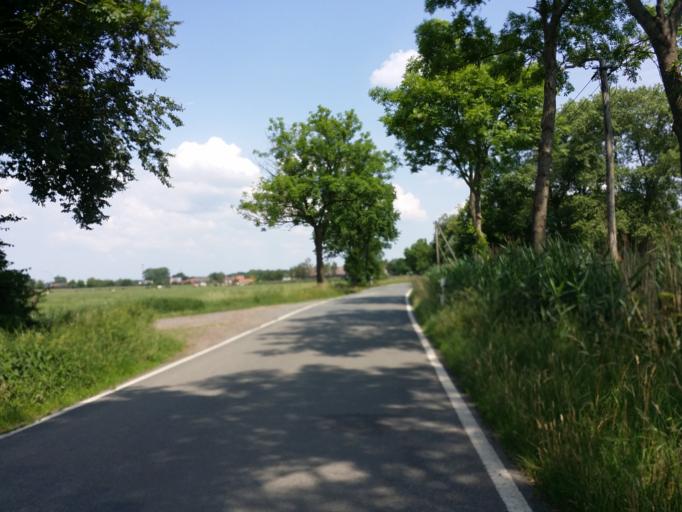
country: DE
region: Lower Saxony
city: Lemwerder
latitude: 53.1580
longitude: 8.5816
